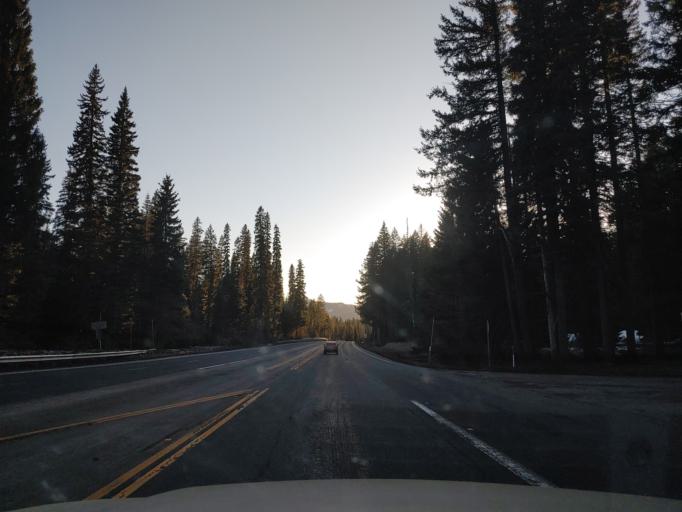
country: US
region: Oregon
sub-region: Lane County
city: Oakridge
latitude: 43.6177
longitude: -122.0826
